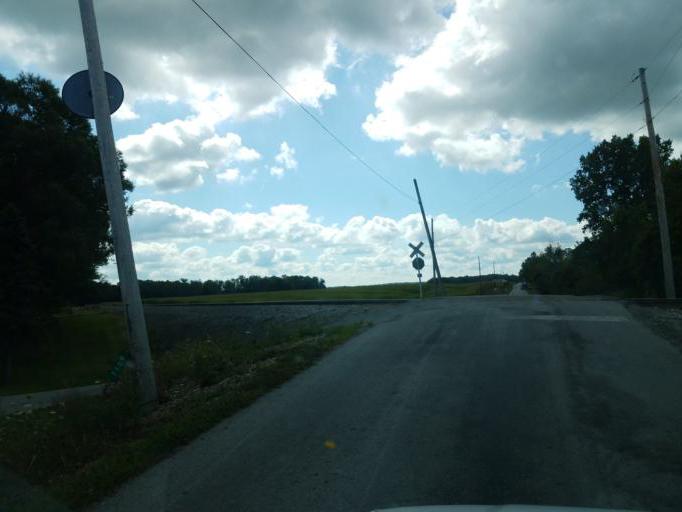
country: US
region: Ohio
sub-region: Medina County
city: Lodi
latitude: 41.0803
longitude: -82.0950
